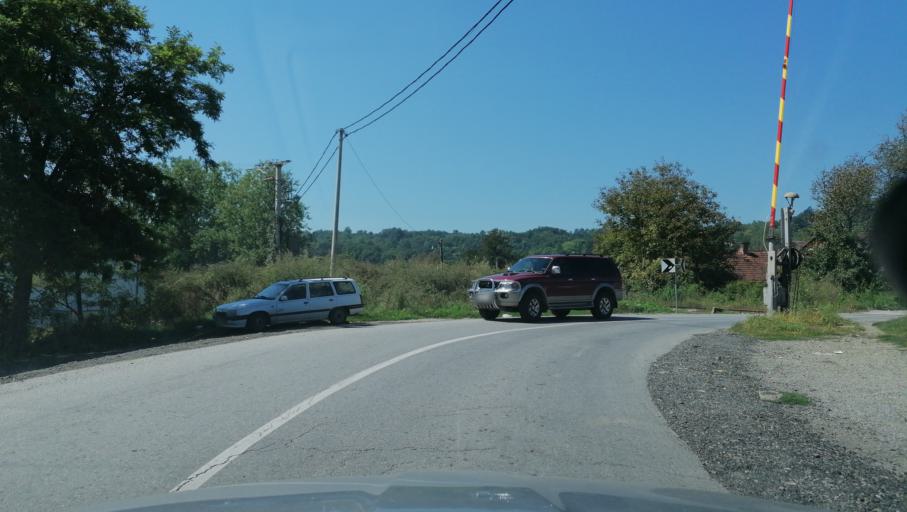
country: RS
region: Central Serbia
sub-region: Raski Okrug
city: Kraljevo
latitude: 43.7252
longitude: 20.7998
